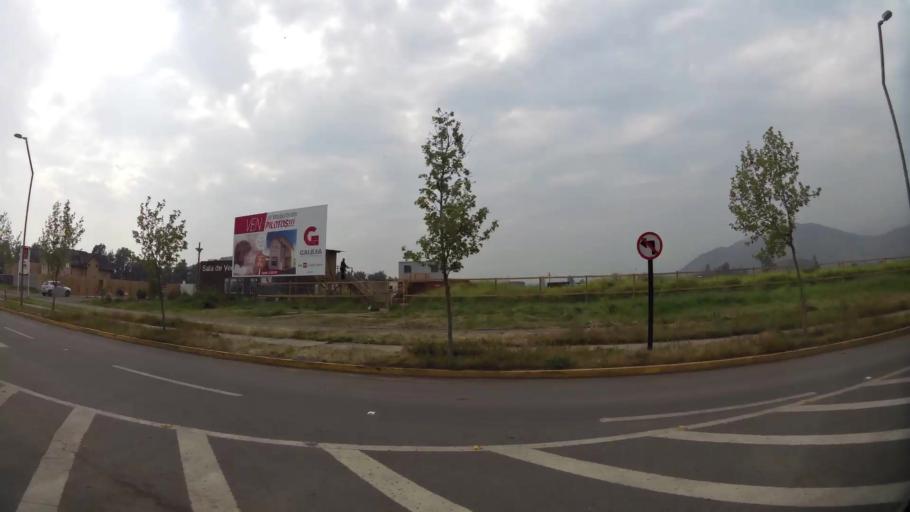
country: CL
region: Santiago Metropolitan
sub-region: Provincia de Chacabuco
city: Chicureo Abajo
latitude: -33.2009
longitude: -70.6572
